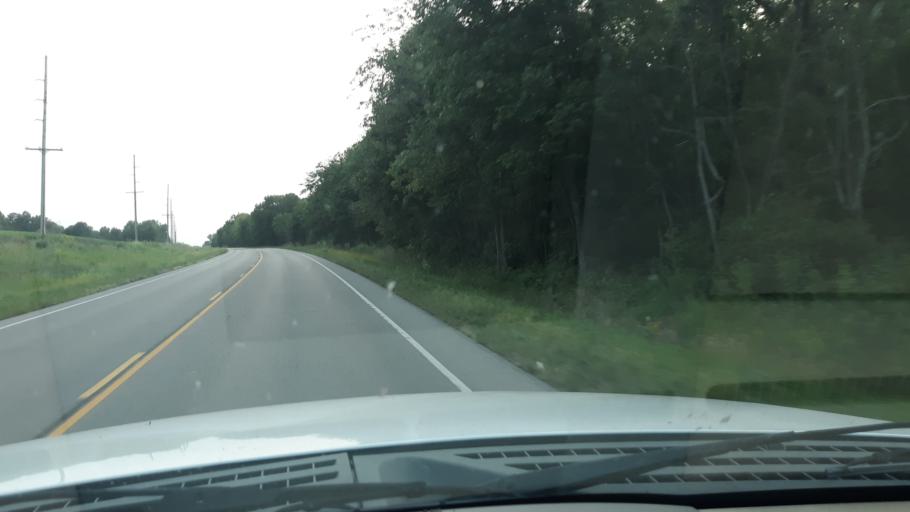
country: US
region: Illinois
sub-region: White County
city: Norris City
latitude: 37.9964
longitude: -88.3017
